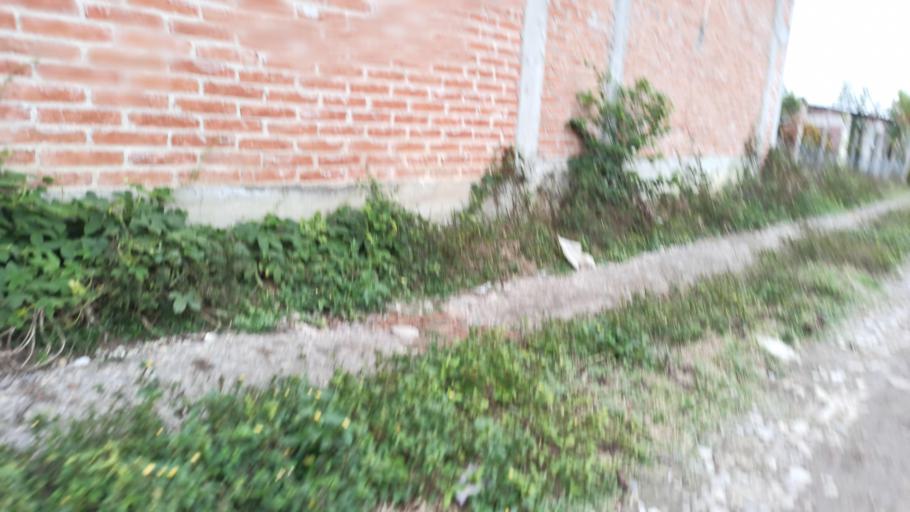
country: MX
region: Veracruz
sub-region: Papantla
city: El Chote
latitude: 20.3992
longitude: -97.3377
